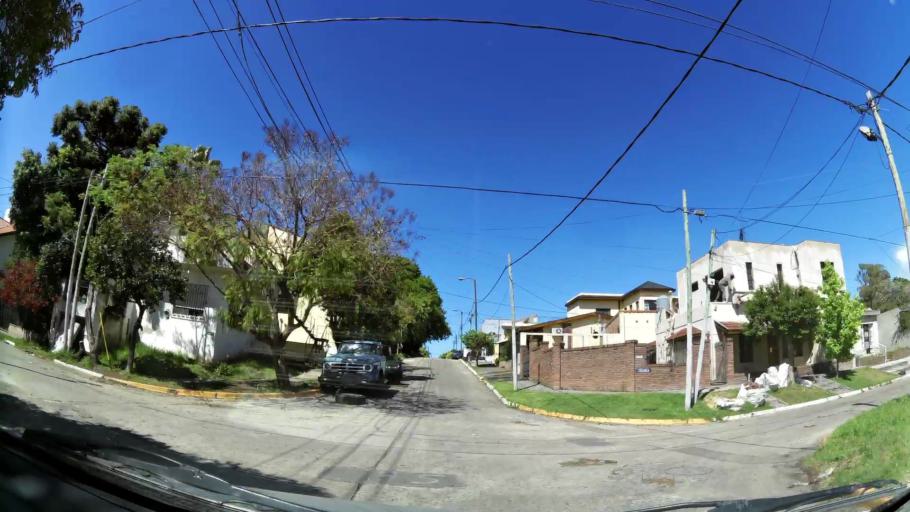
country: AR
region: Buenos Aires
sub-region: Partido de Quilmes
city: Quilmes
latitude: -34.7021
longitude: -58.2854
